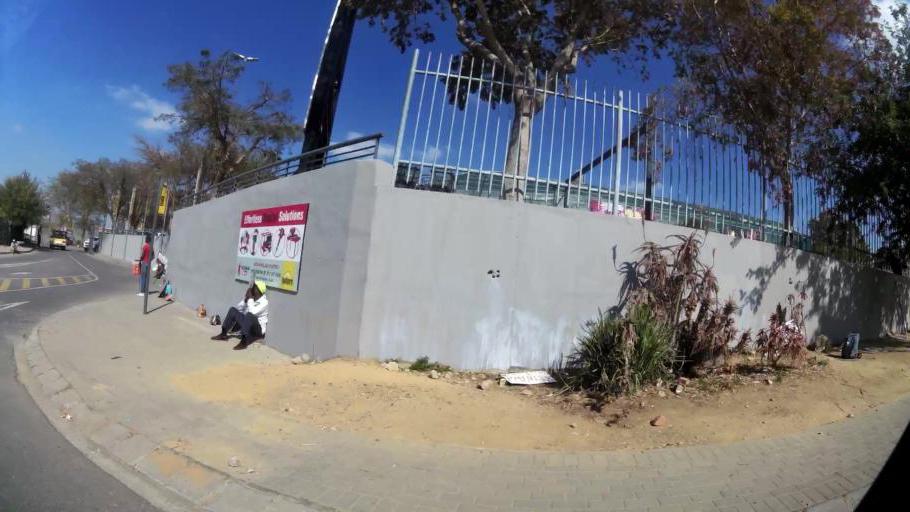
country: ZA
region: Gauteng
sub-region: West Rand District Municipality
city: Muldersdriseloop
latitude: -26.0540
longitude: 27.9539
